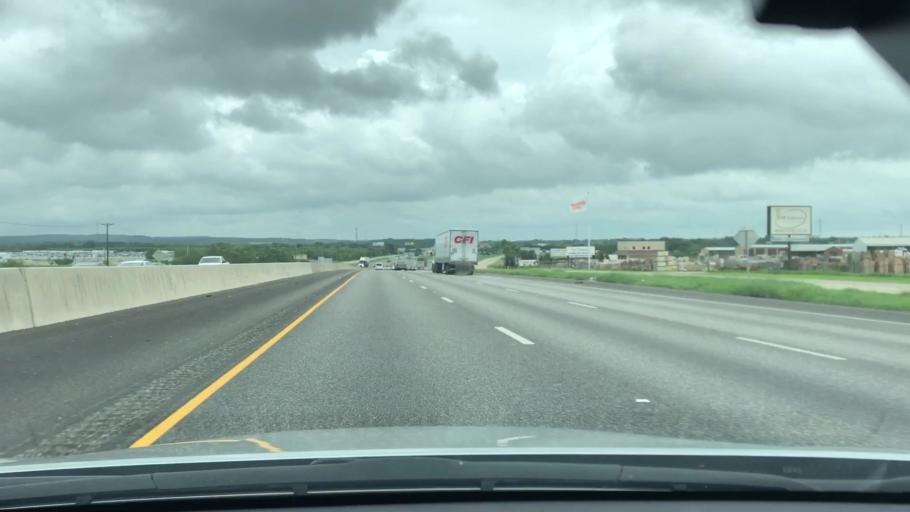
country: US
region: Texas
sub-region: Guadalupe County
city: Lake Dunlap
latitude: 29.7848
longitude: -98.0301
